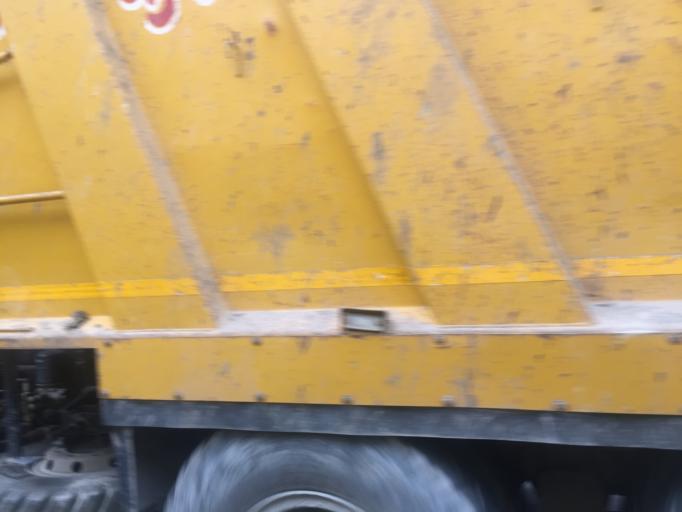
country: IN
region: Maharashtra
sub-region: Thane
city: Airoli
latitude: 19.1534
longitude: 72.9930
